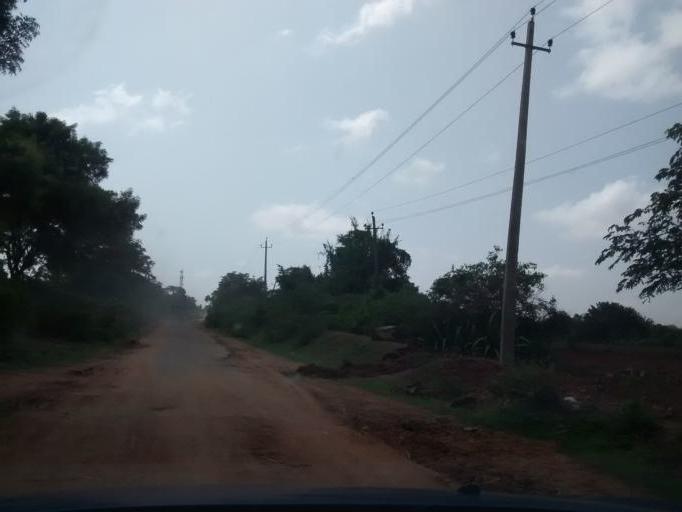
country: IN
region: Karnataka
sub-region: Hassan
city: Hole Narsipur
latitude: 12.6920
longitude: 76.1866
